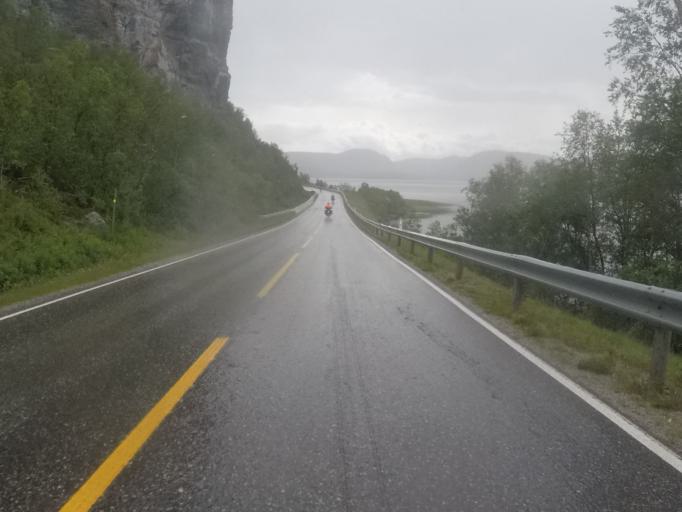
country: NO
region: Finnmark Fylke
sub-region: Porsanger
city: Lakselv
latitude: 69.8571
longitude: 25.0500
